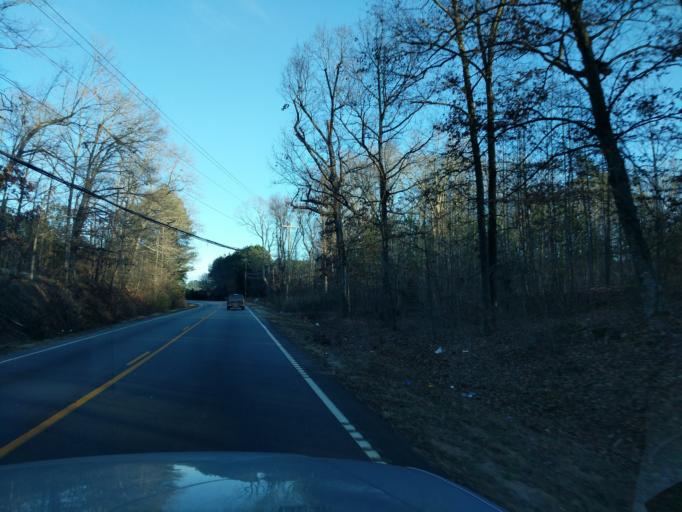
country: US
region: South Carolina
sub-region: Greenville County
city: Fountain Inn
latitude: 34.6740
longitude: -82.2248
